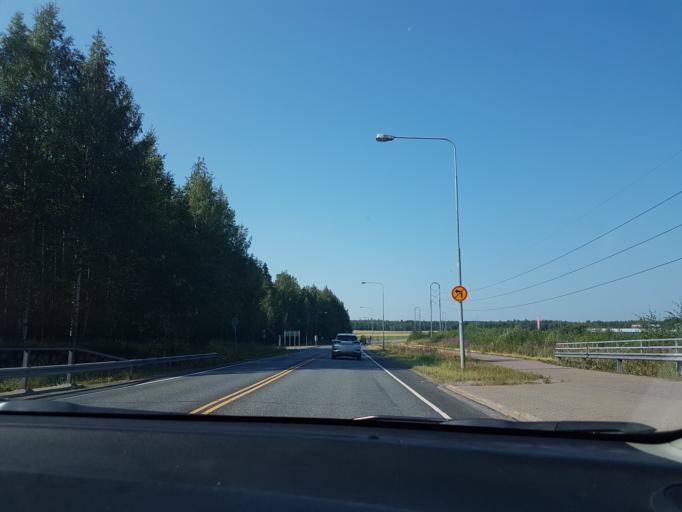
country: FI
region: Uusimaa
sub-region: Helsinki
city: Tuusula
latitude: 60.3773
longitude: 25.0540
